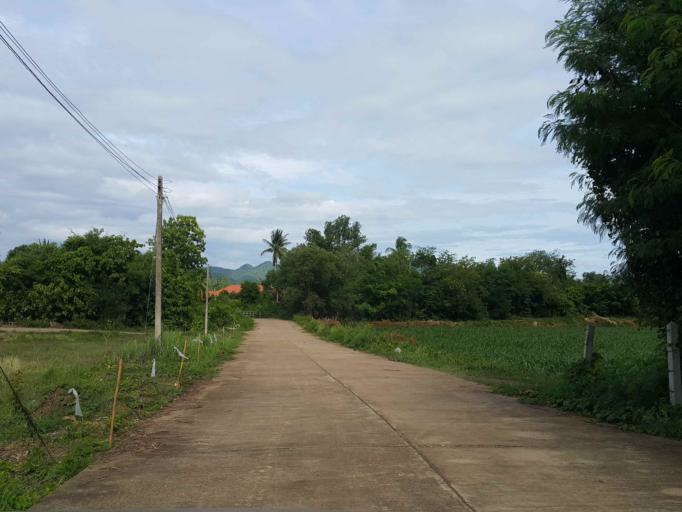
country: TH
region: Sukhothai
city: Thung Saliam
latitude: 17.2278
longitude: 99.5272
